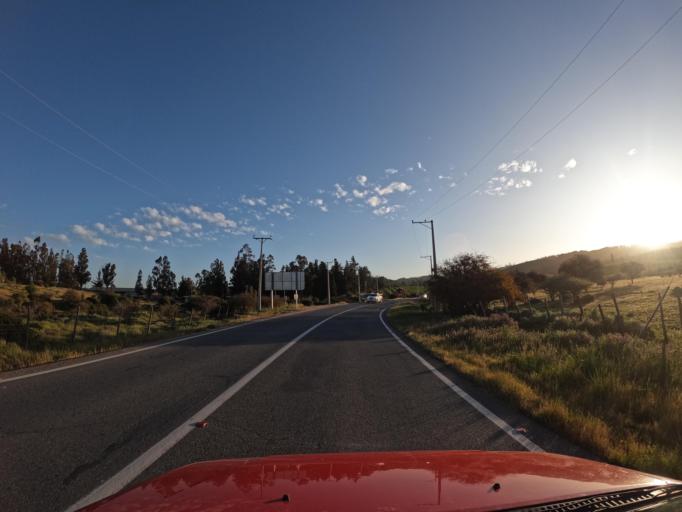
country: CL
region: O'Higgins
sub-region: Provincia de Colchagua
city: Santa Cruz
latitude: -34.3307
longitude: -71.7462
